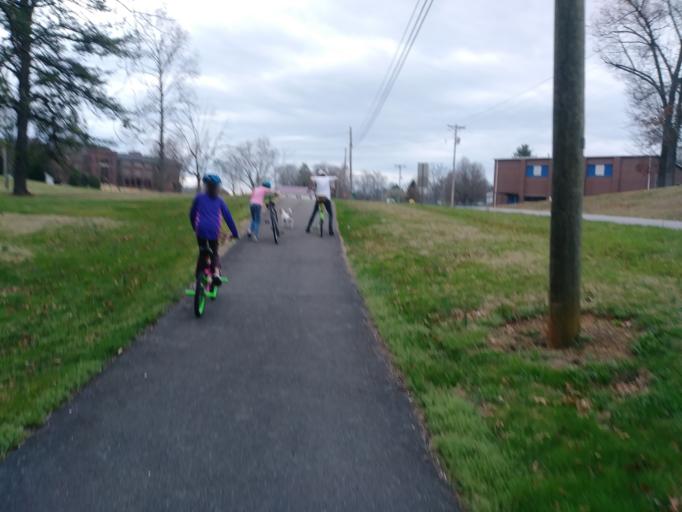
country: US
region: Tennessee
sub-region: Greene County
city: Tusculum
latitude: 36.1770
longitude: -82.7557
